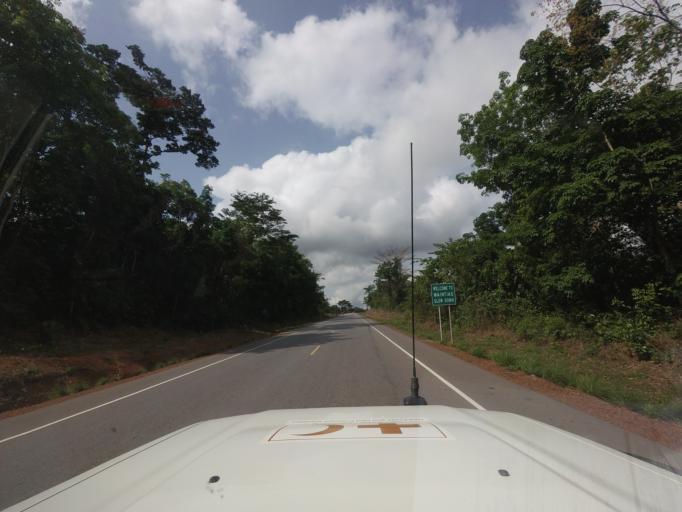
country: LR
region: Nimba
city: Sanniquellie
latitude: 7.1457
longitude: -9.0557
